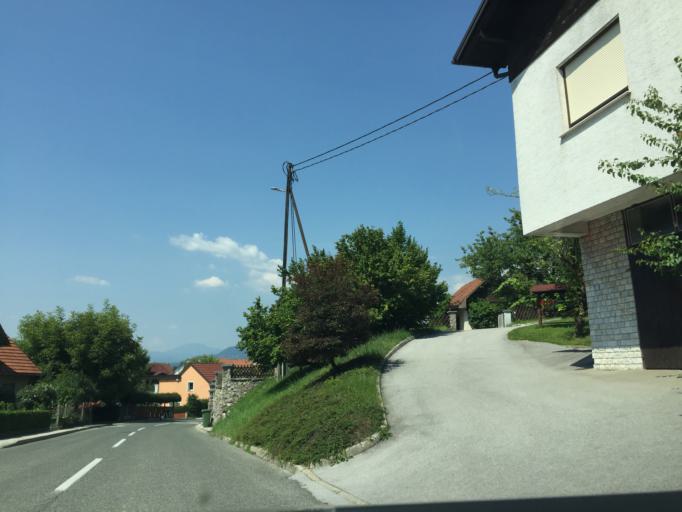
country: SI
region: Prebold
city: Prebold
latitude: 46.2335
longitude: 15.0951
